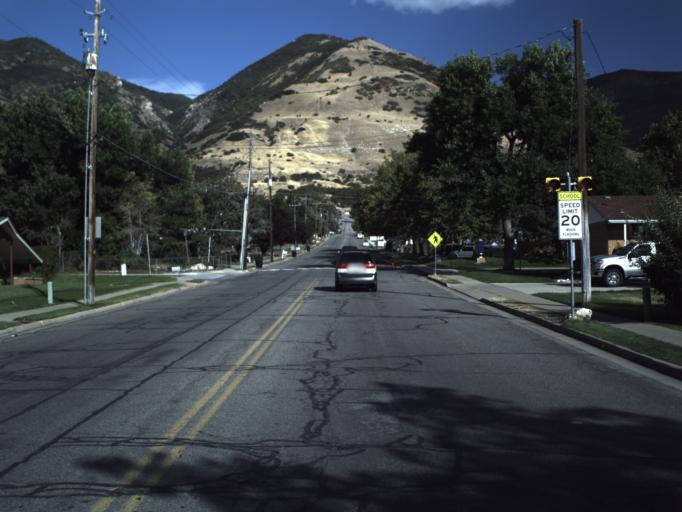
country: US
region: Utah
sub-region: Davis County
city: Centerville
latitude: 40.9215
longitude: -111.8780
